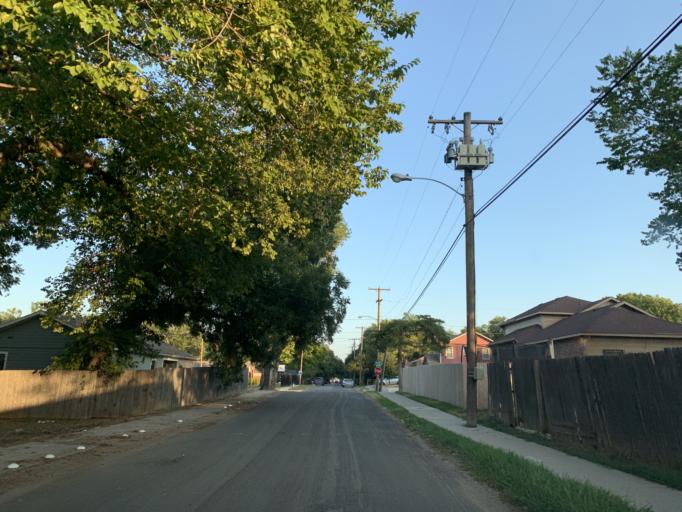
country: US
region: Texas
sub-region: Dallas County
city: Dallas
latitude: 32.7041
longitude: -96.7826
